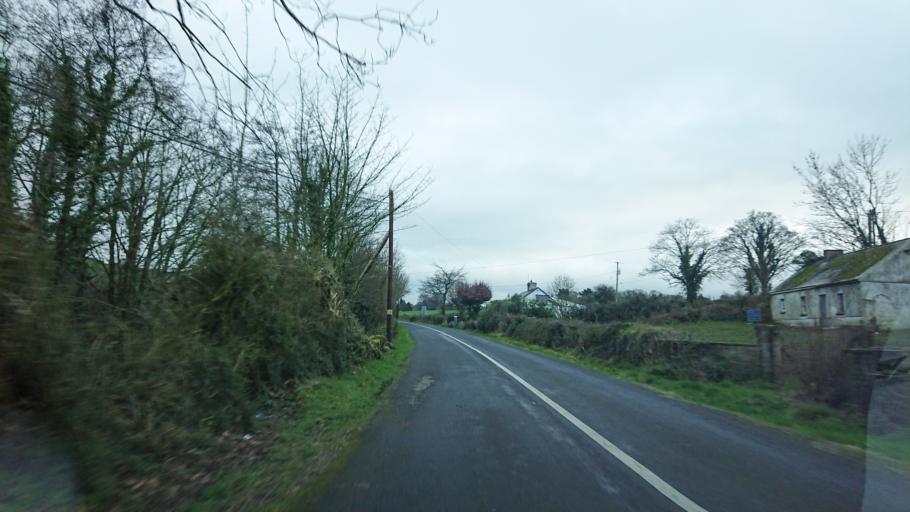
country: IE
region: Munster
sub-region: Waterford
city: Portlaw
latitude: 52.2793
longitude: -7.3900
